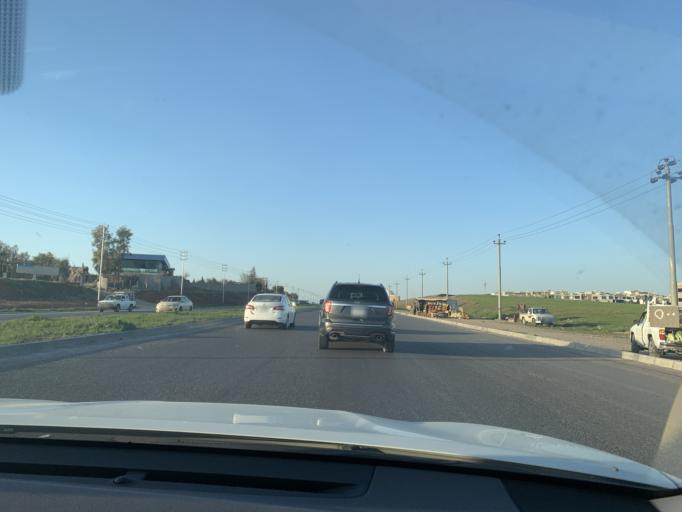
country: IQ
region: Arbil
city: Erbil
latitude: 36.2744
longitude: 44.0154
